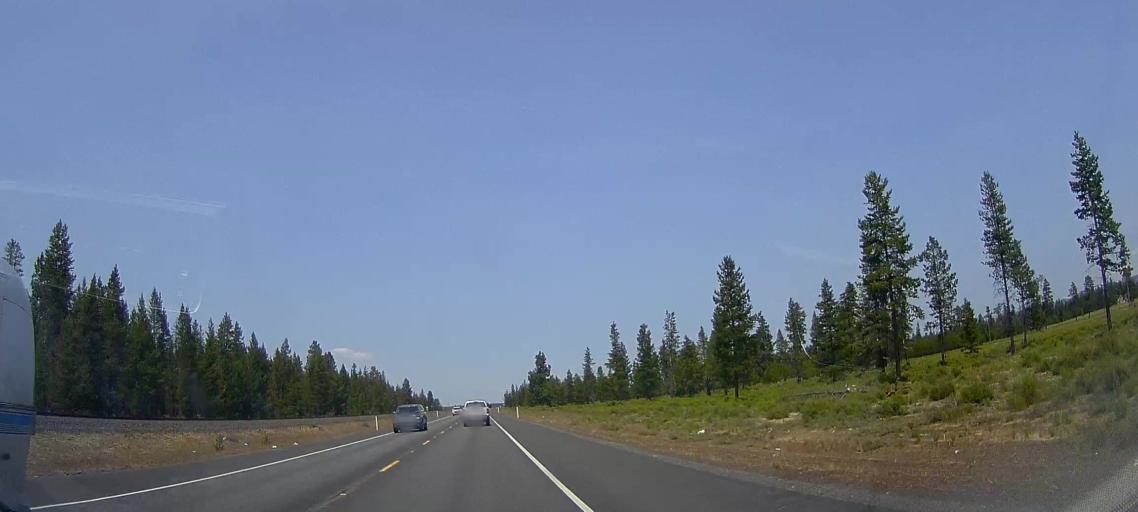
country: US
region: Oregon
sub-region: Deschutes County
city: La Pine
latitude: 43.7328
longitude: -121.4690
